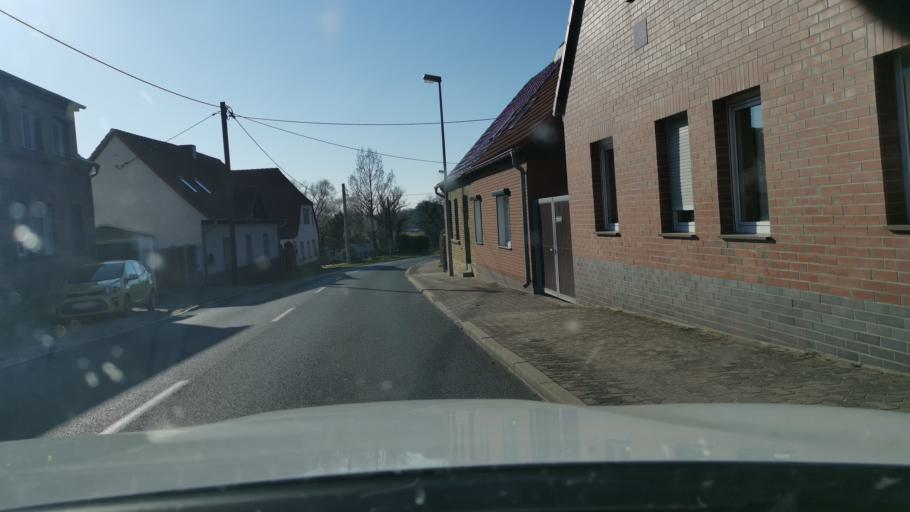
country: DE
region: Saxony-Anhalt
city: Muldenstein
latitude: 51.6801
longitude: 12.3273
